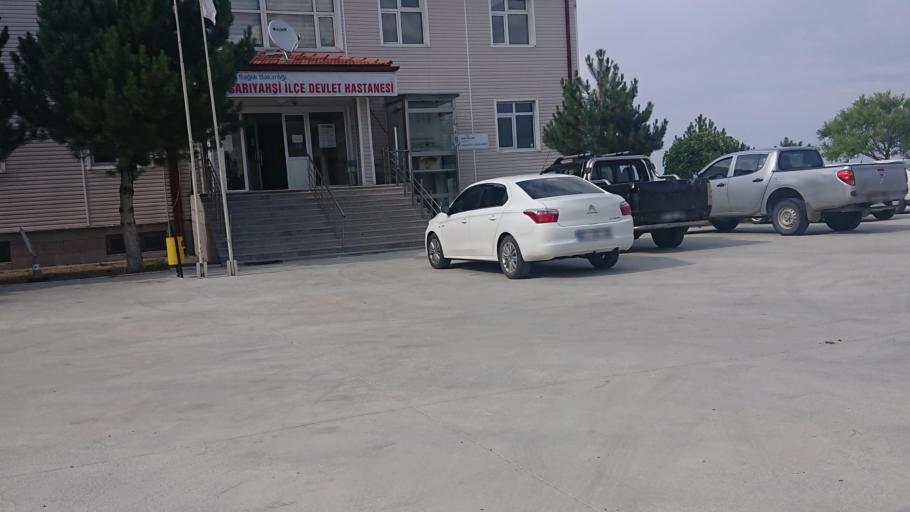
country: TR
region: Aksaray
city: Sariyahsi
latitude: 38.9724
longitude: 33.8322
